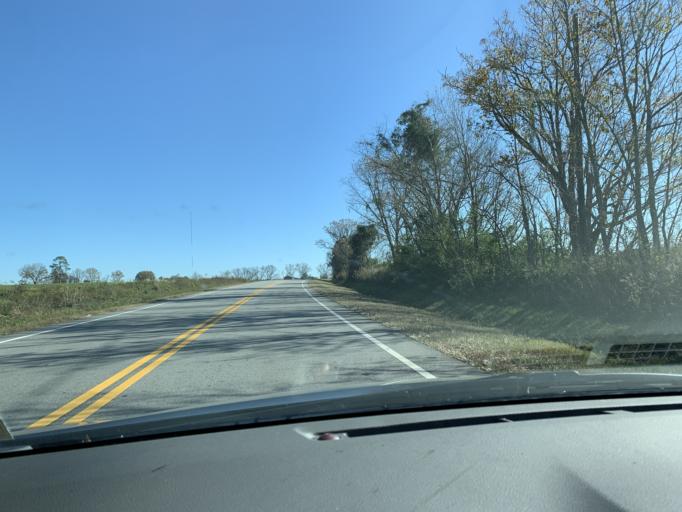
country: US
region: Georgia
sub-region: Ben Hill County
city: Fitzgerald
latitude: 31.7145
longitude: -83.1814
